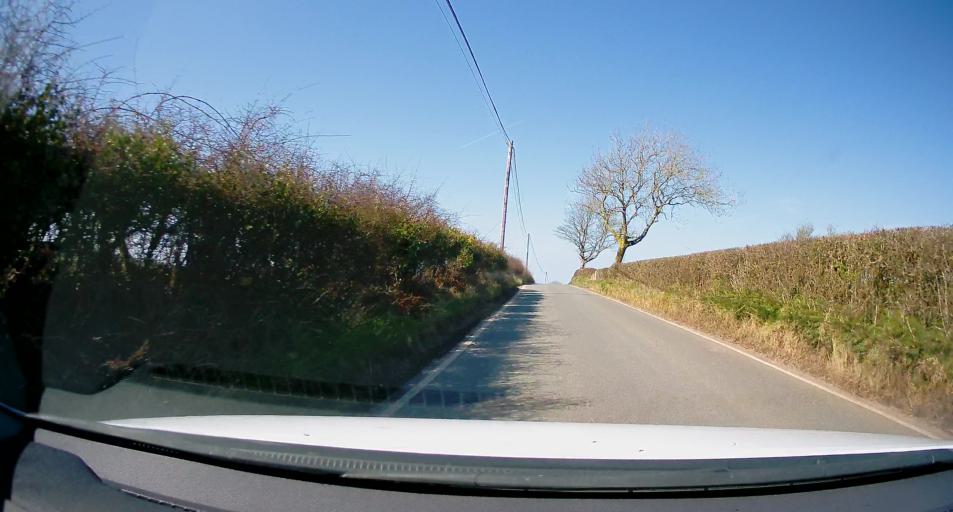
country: GB
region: Wales
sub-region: County of Ceredigion
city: Penparcau
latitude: 52.3220
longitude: -4.0661
